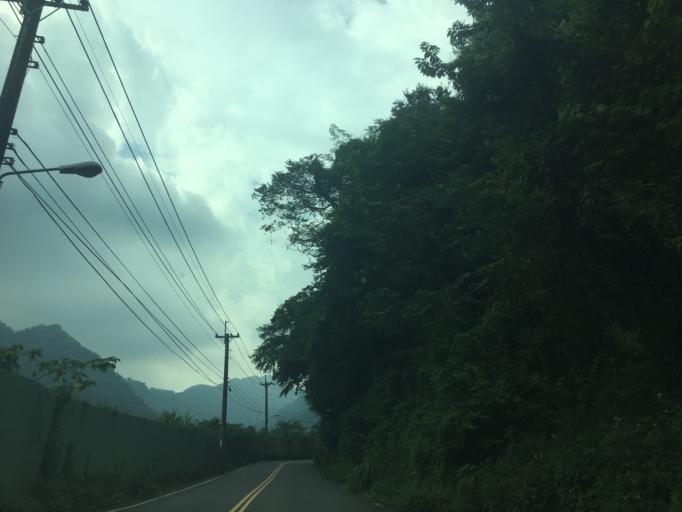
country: TW
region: Taiwan
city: Fengyuan
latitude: 24.3319
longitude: 120.9205
